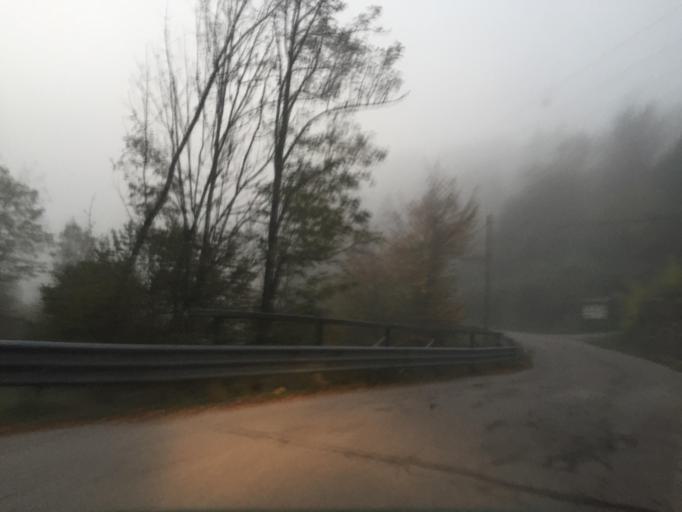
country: IT
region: Friuli Venezia Giulia
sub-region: Provincia di Pordenone
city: Andreis
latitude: 46.2016
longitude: 12.6232
